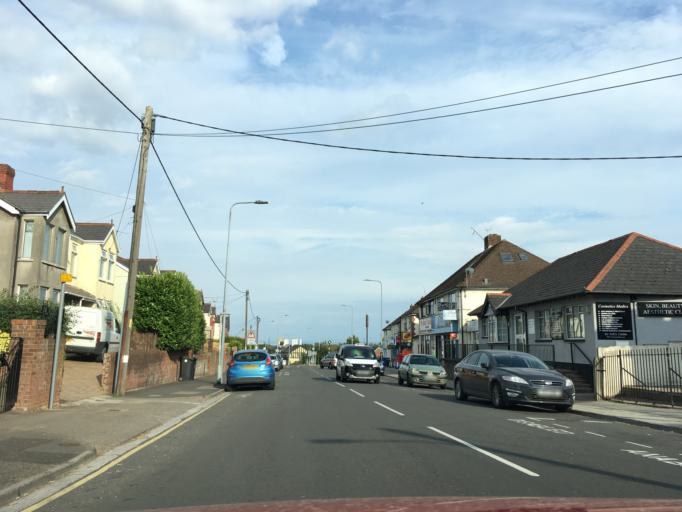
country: GB
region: Wales
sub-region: Cardiff
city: Cardiff
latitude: 51.5050
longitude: -3.1286
